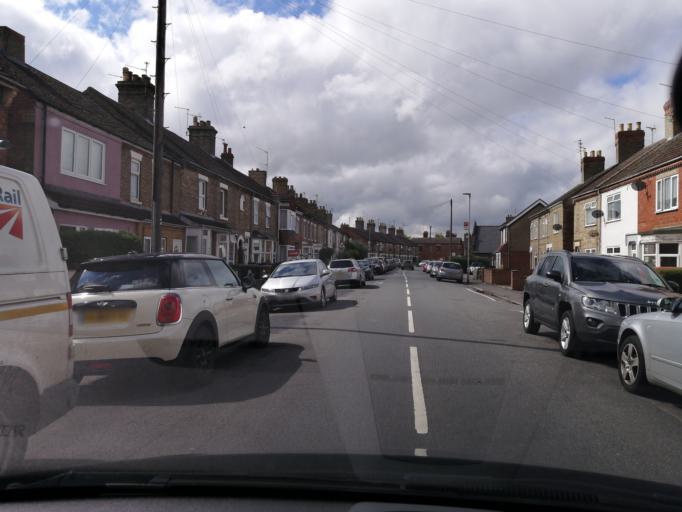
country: GB
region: England
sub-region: Peterborough
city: Peterborough
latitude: 52.5617
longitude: -0.2532
